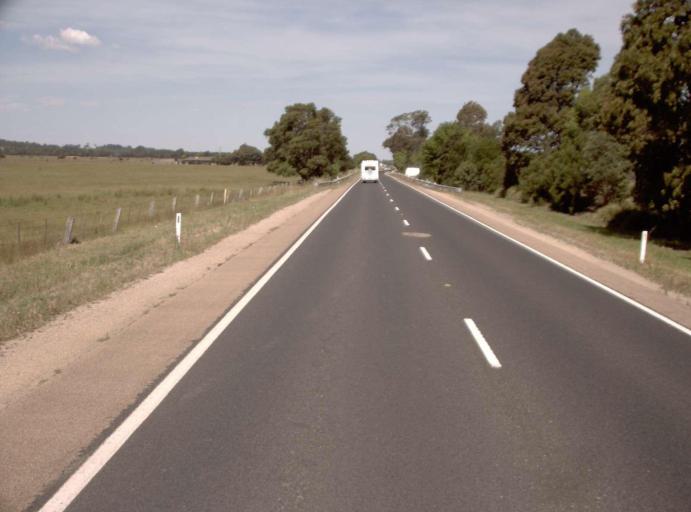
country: AU
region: Victoria
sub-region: East Gippsland
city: Bairnsdale
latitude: -37.8206
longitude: 147.6649
